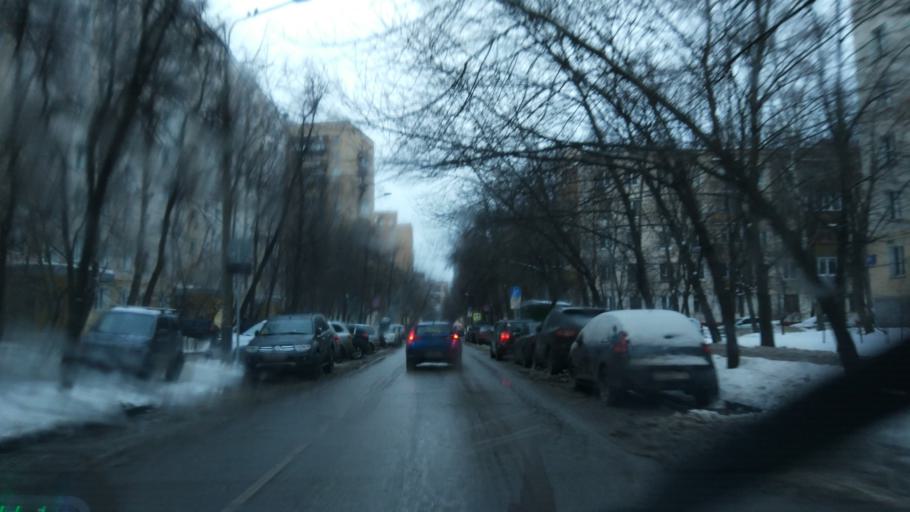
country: RU
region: Moskovskaya
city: Izmaylovo
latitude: 55.7911
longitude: 37.8025
